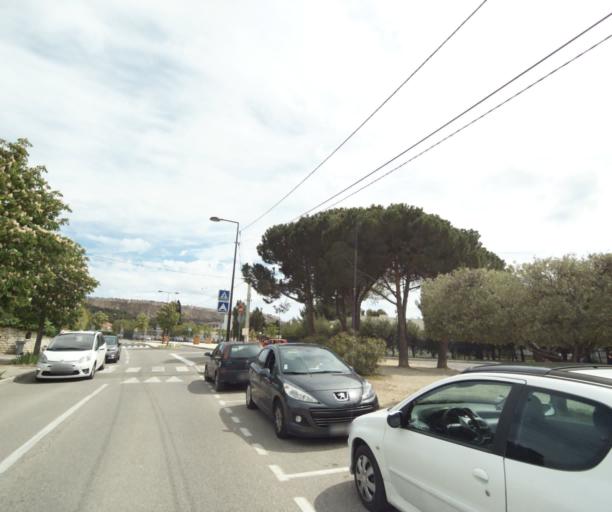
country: FR
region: Provence-Alpes-Cote d'Azur
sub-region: Departement des Bouches-du-Rhone
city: Rognac
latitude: 43.4846
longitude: 5.2346
